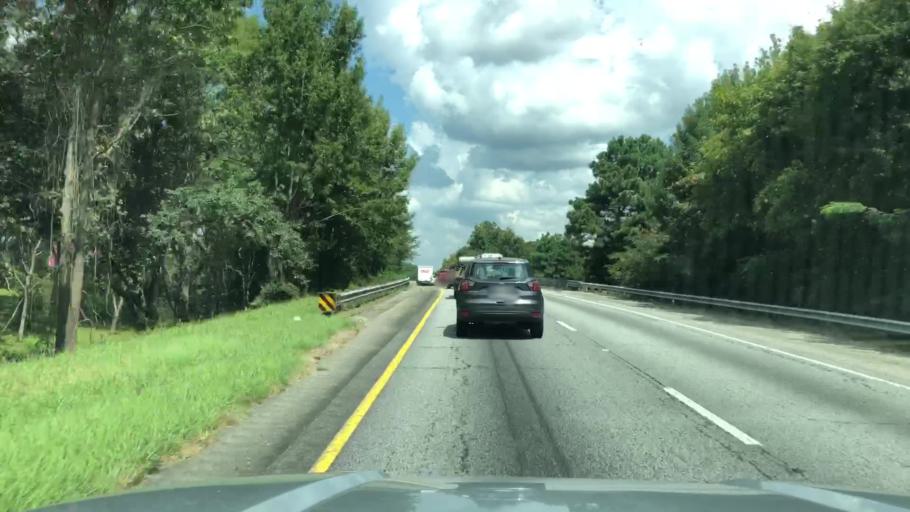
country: US
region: Georgia
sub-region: Fulton County
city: College Park
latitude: 33.6222
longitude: -84.4873
